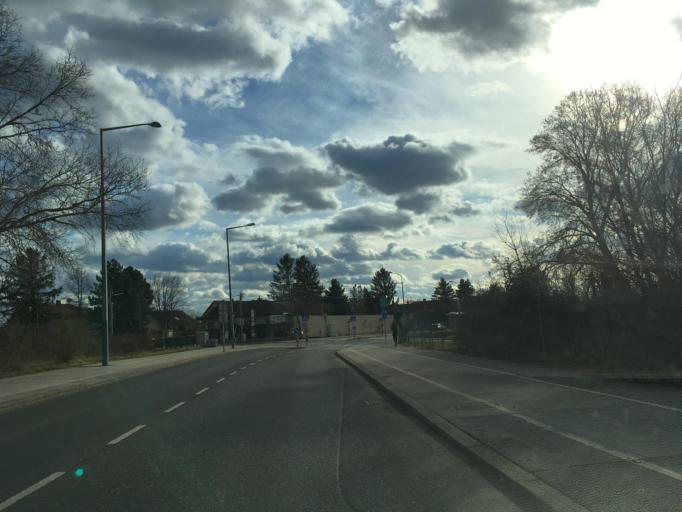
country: AT
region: Lower Austria
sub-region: Politischer Bezirk Wien-Umgebung
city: Schwechat
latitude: 48.2049
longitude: 16.4761
